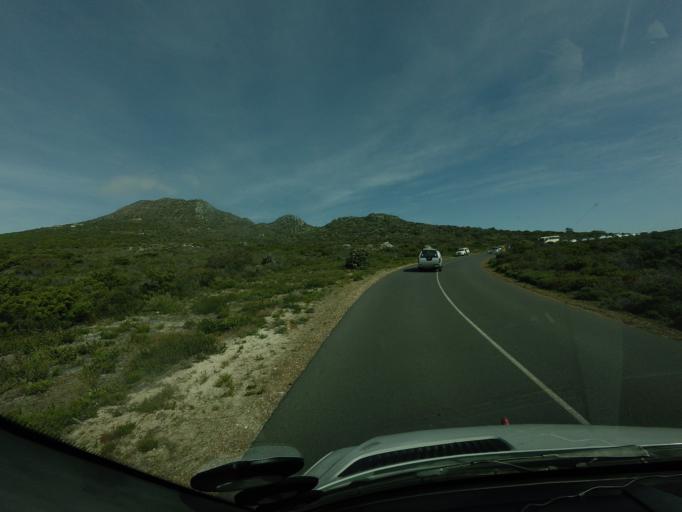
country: ZA
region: Western Cape
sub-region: City of Cape Town
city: Retreat
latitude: -34.3413
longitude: 18.4673
